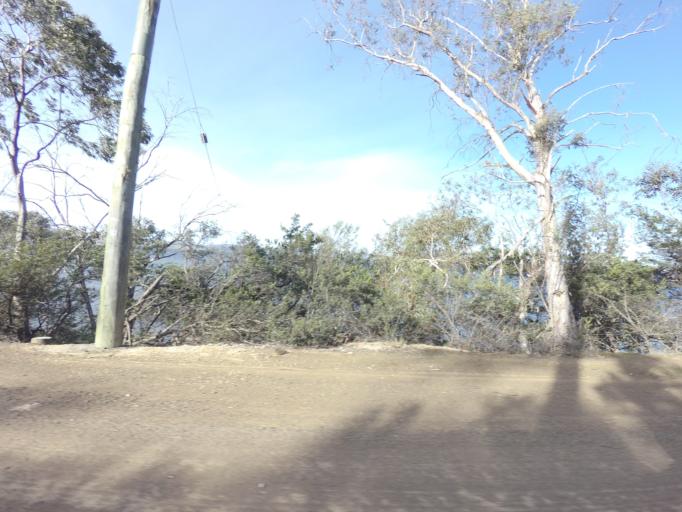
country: AU
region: Tasmania
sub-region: Kingborough
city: Kettering
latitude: -43.1156
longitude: 147.2713
